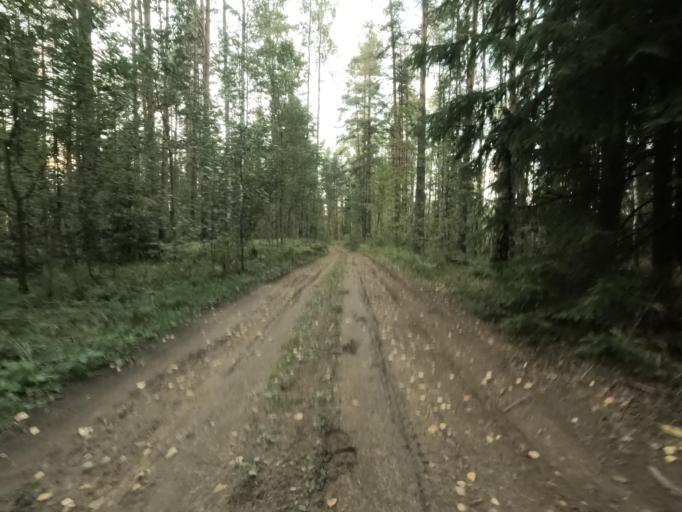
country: RU
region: Leningrad
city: Otradnoye
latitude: 59.8375
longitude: 30.8059
